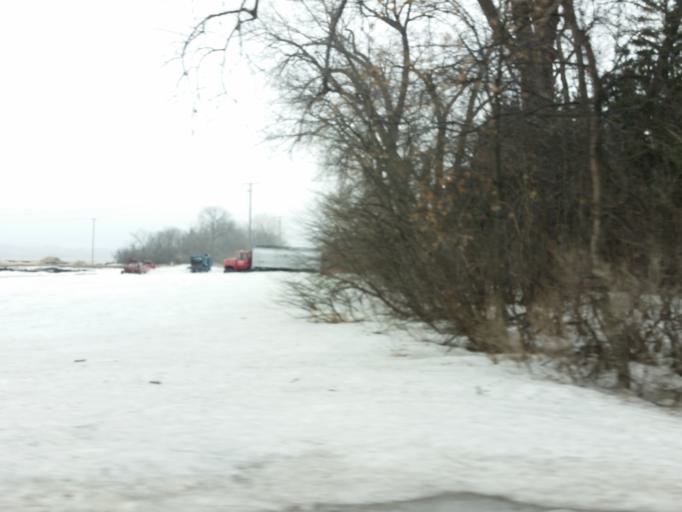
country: US
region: North Dakota
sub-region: Walsh County
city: Grafton
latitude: 48.6237
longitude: -97.4489
